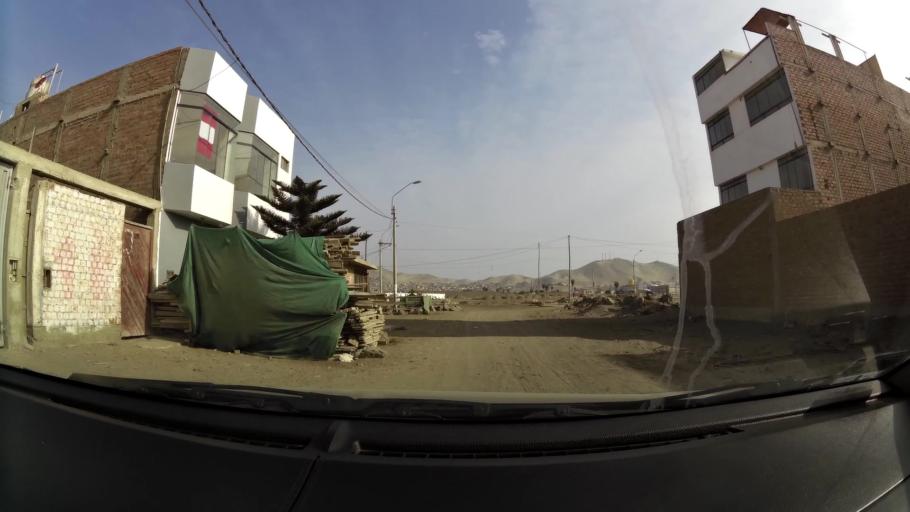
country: PE
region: Lima
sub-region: Lima
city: Santa Rosa
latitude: -11.7637
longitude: -77.1681
